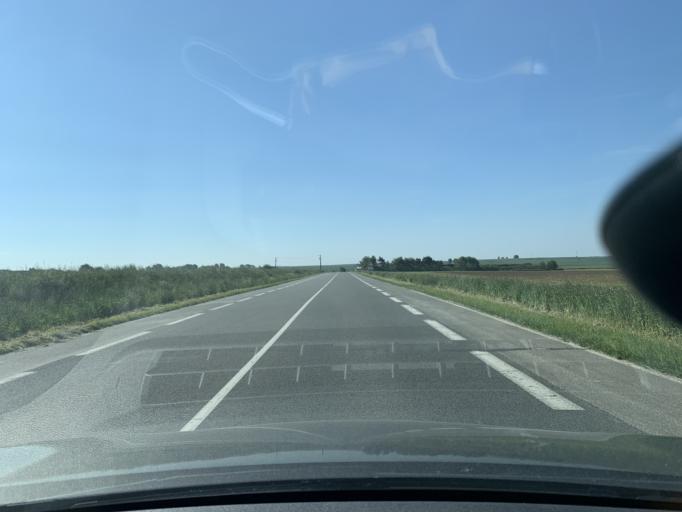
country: FR
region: Nord-Pas-de-Calais
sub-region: Departement du Nord
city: Cambrai
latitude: 50.1429
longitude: 3.2448
